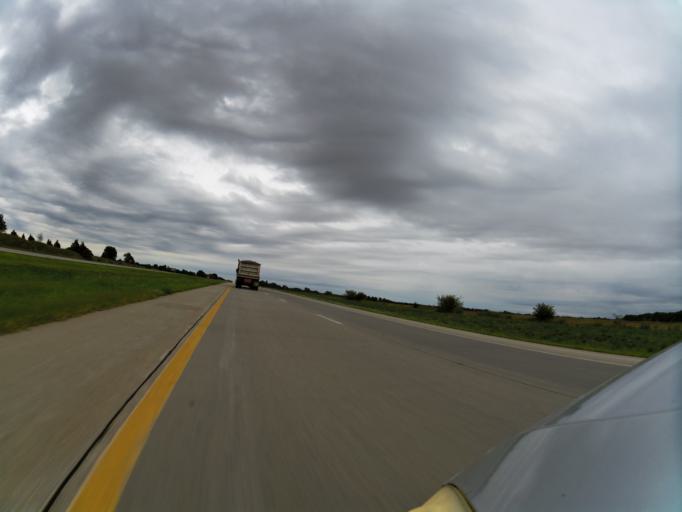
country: US
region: Kansas
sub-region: Reno County
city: Haven
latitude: 37.9329
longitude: -97.8565
